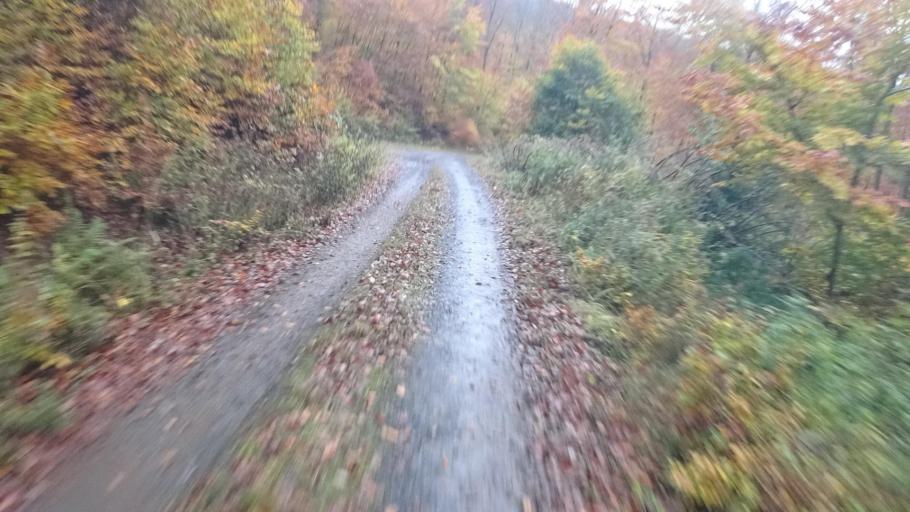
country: DE
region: Rheinland-Pfalz
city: Utzenhain
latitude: 50.1331
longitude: 7.6668
